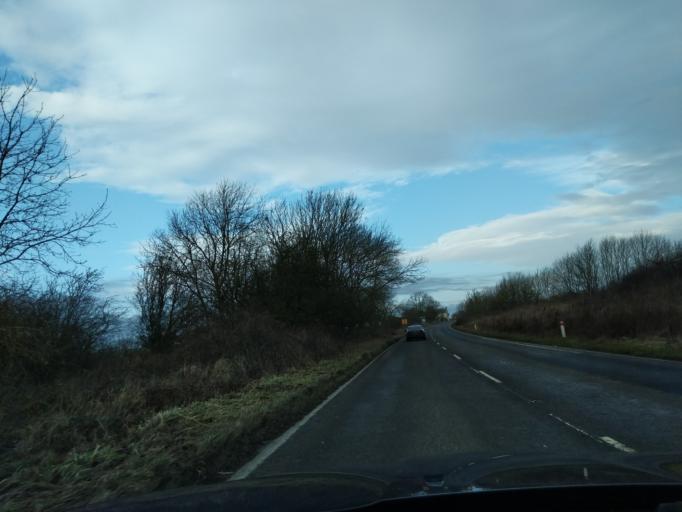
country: GB
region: England
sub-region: Northumberland
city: Meldon
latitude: 55.0813
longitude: -1.8067
